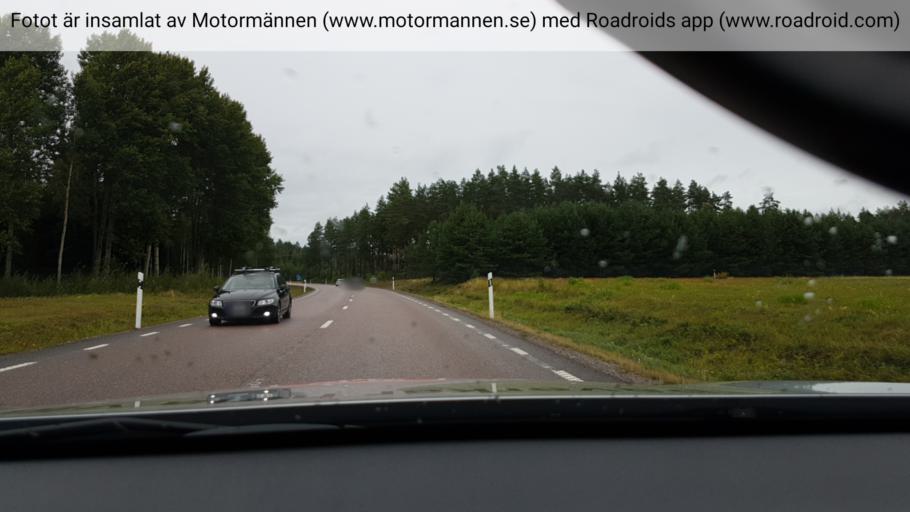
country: SE
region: Gaevleborg
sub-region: Gavle Kommun
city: Hedesunda
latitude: 60.4155
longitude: 16.9789
